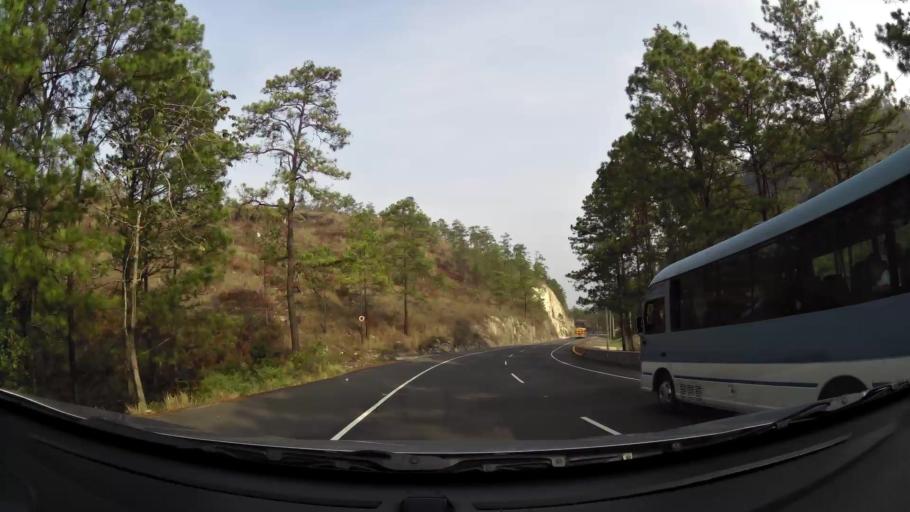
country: HN
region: Francisco Morazan
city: Zambrano
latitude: 14.2884
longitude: -87.4764
